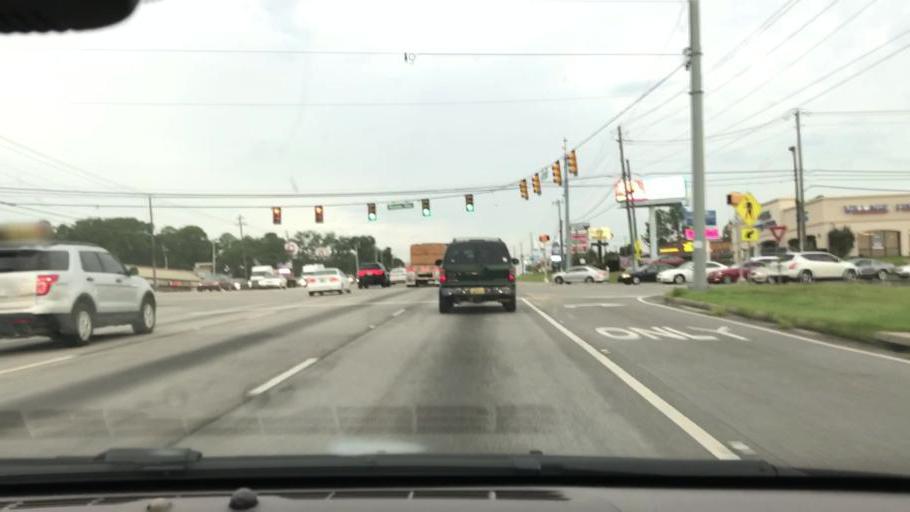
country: US
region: Alabama
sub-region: Houston County
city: Dothan
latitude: 31.2571
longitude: -85.4330
